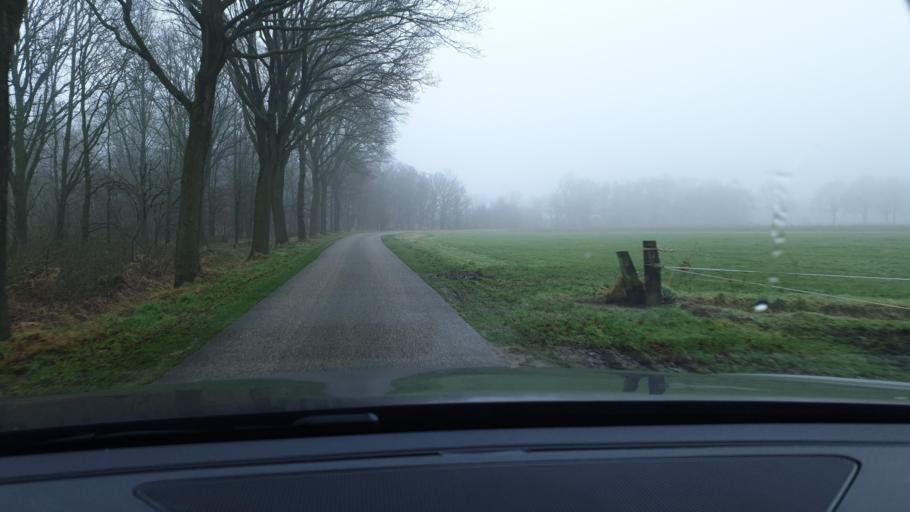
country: NL
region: North Brabant
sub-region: Gemeente Asten
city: Asten
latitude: 51.3617
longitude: 5.8437
